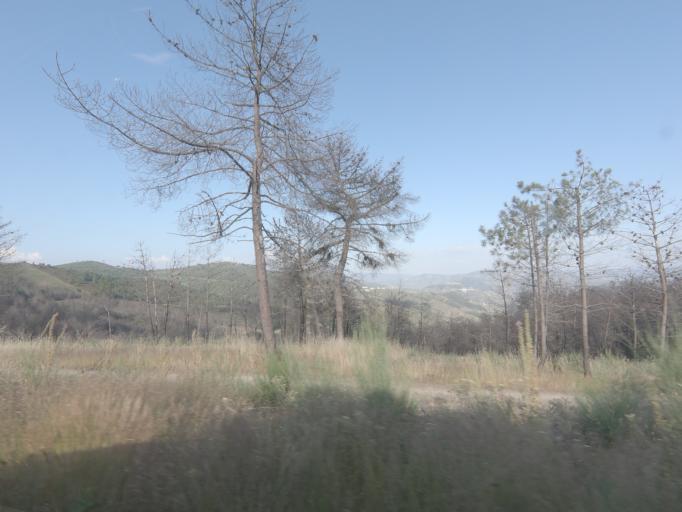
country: PT
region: Vila Real
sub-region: Sabrosa
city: Vilela
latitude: 41.2211
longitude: -7.5994
